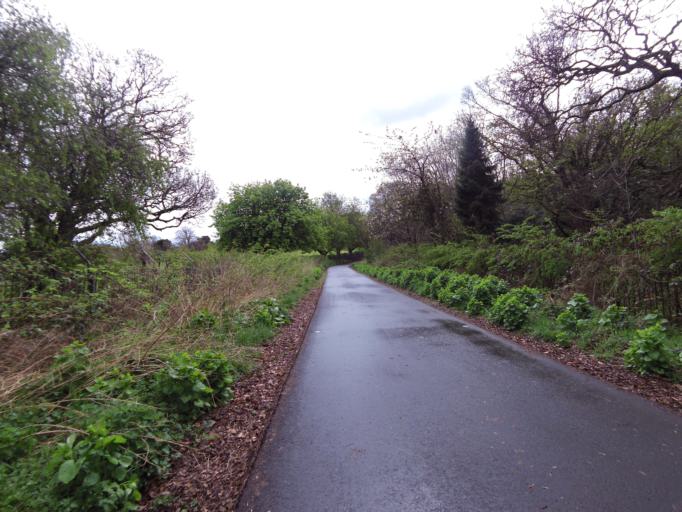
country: GB
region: Scotland
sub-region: Edinburgh
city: Currie
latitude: 55.9679
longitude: -3.2966
